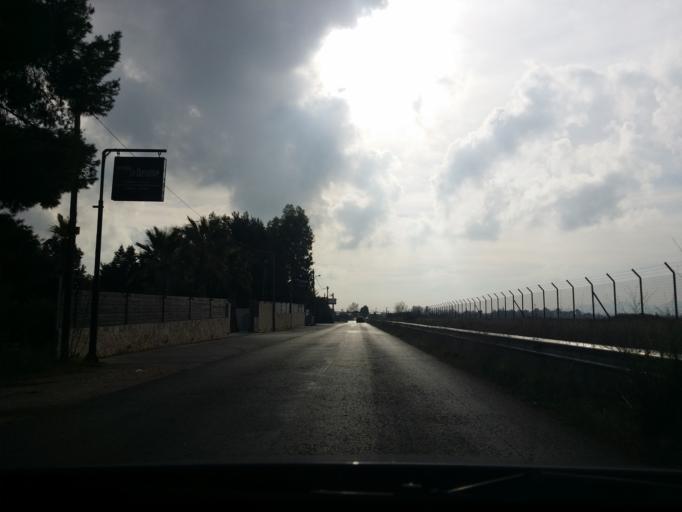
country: GR
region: Attica
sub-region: Nomarchia Anatolikis Attikis
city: Varybobi
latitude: 38.1084
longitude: 23.7900
